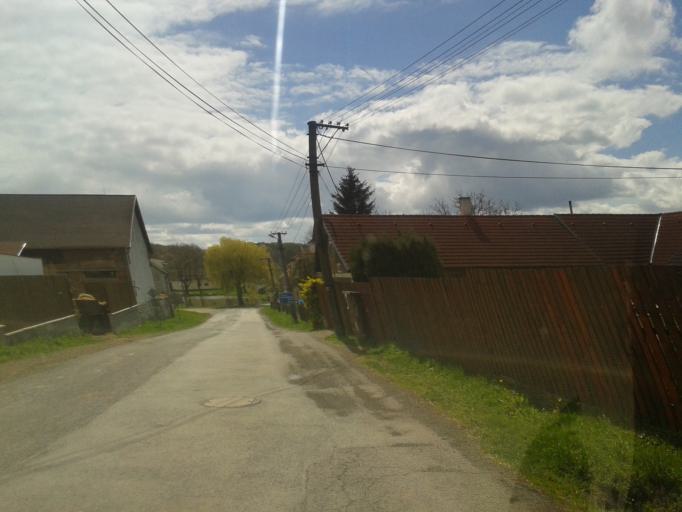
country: CZ
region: Plzensky
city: Zbiroh
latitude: 49.8861
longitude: 13.8042
